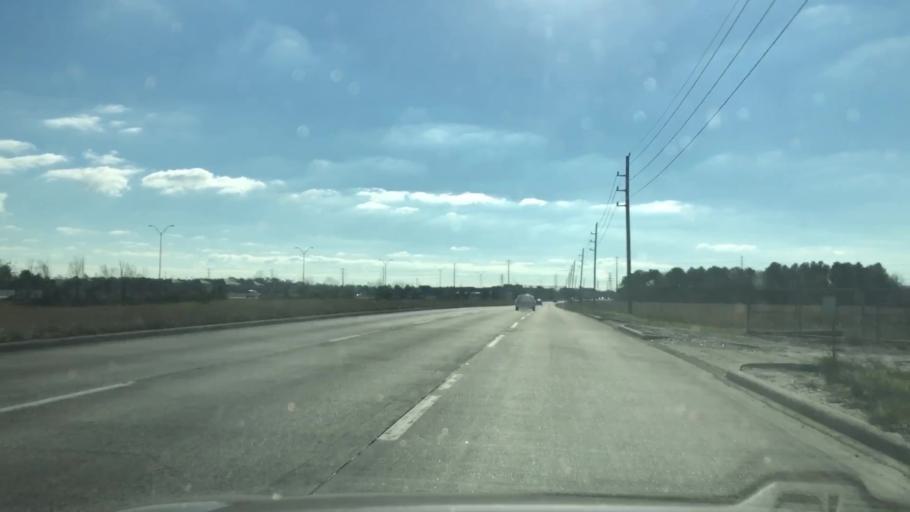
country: US
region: Texas
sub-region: Harris County
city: Cloverleaf
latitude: 29.8269
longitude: -95.1716
